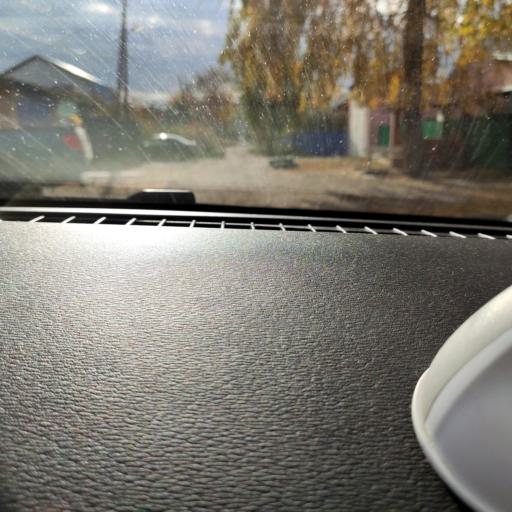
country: RU
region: Samara
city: Petra-Dubrava
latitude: 53.2512
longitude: 50.3125
